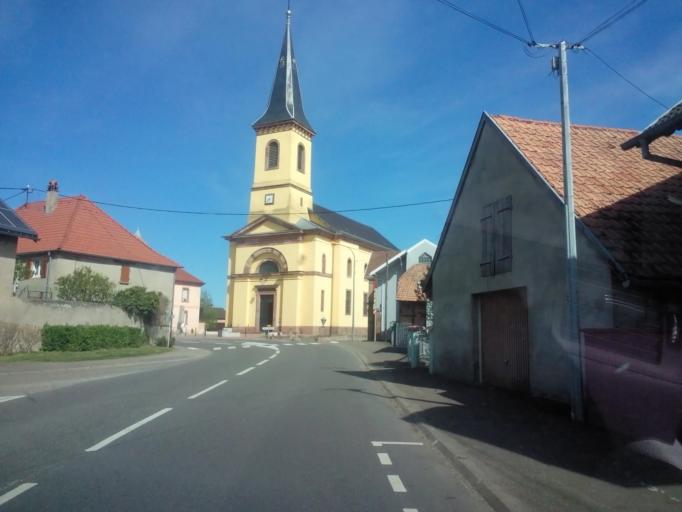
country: FR
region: Alsace
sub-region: Departement du Haut-Rhin
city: Algolsheim
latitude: 47.9698
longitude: 7.5387
